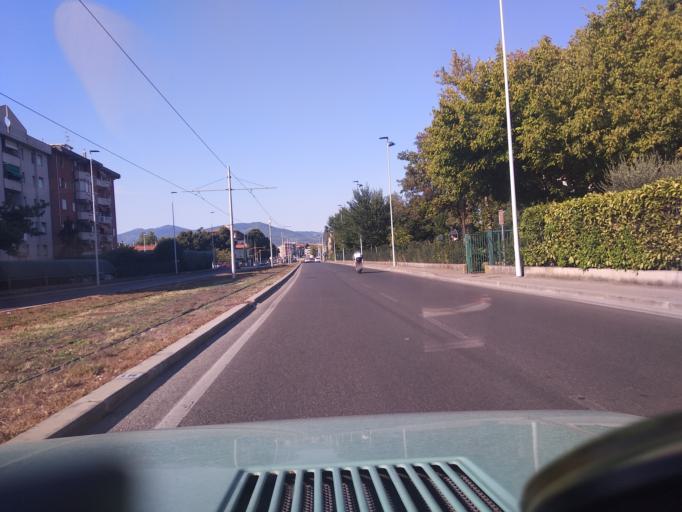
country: IT
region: Tuscany
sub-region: Province of Florence
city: Scandicci
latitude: 43.7687
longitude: 11.2103
